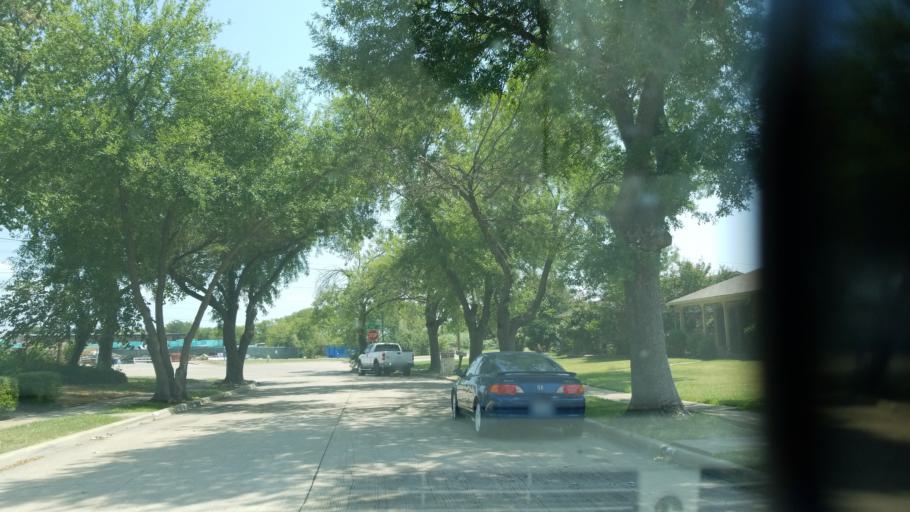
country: US
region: Texas
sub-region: Dallas County
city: Garland
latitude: 32.9285
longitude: -96.6313
